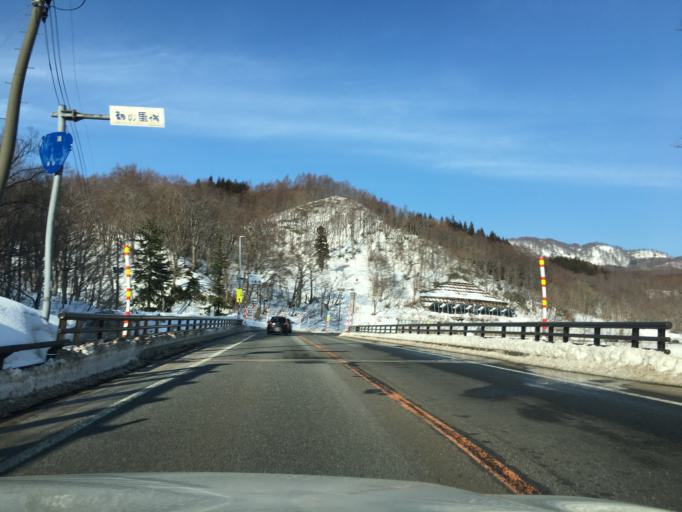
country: JP
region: Yamagata
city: Tsuruoka
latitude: 38.5800
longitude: 139.9363
